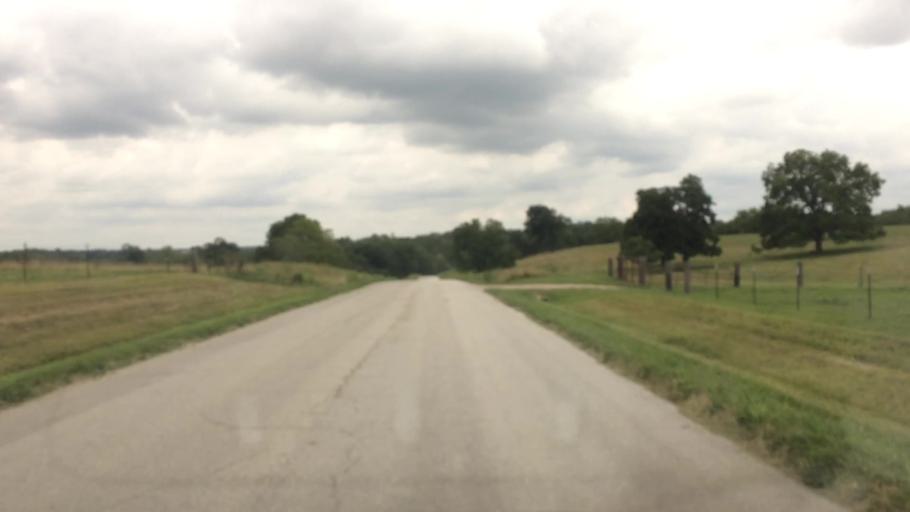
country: US
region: Missouri
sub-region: Greene County
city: Strafford
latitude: 37.3049
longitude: -93.0748
